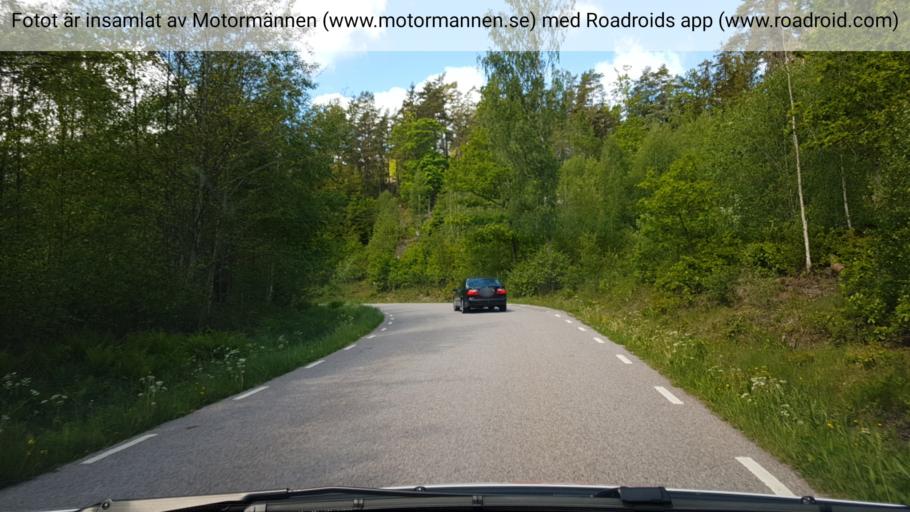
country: SE
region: Kalmar
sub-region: Vasterviks Kommun
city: Forserum
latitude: 57.9246
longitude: 16.4526
